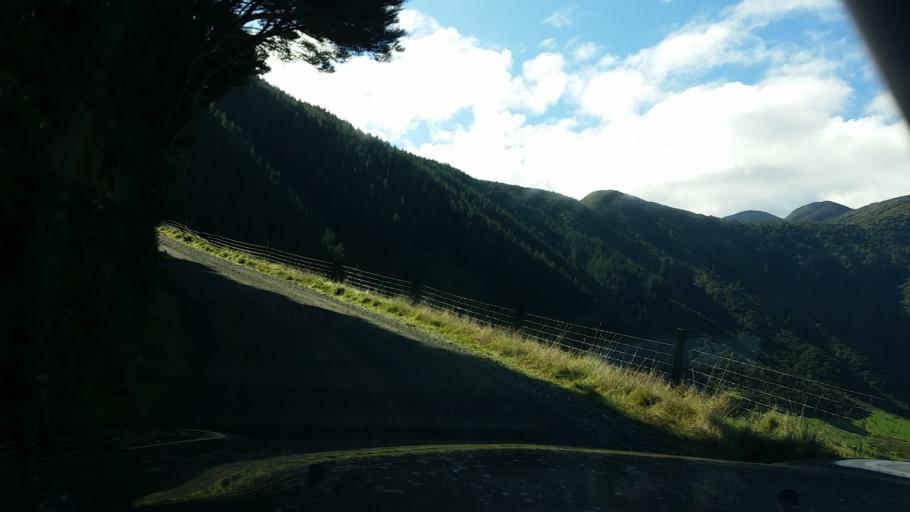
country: NZ
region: Marlborough
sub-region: Marlborough District
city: Picton
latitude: -41.1439
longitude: 174.0506
